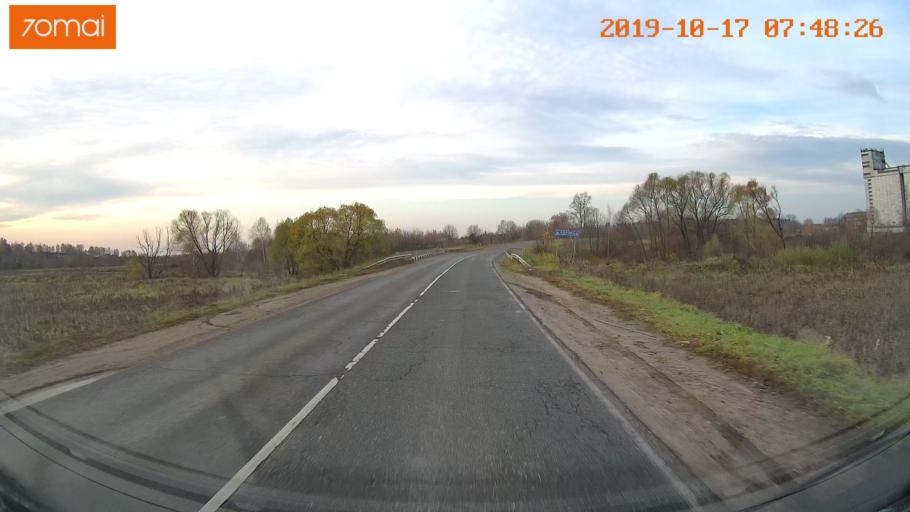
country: RU
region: Vladimir
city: Yur'yev-Pol'skiy
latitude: 56.4797
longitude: 39.6754
